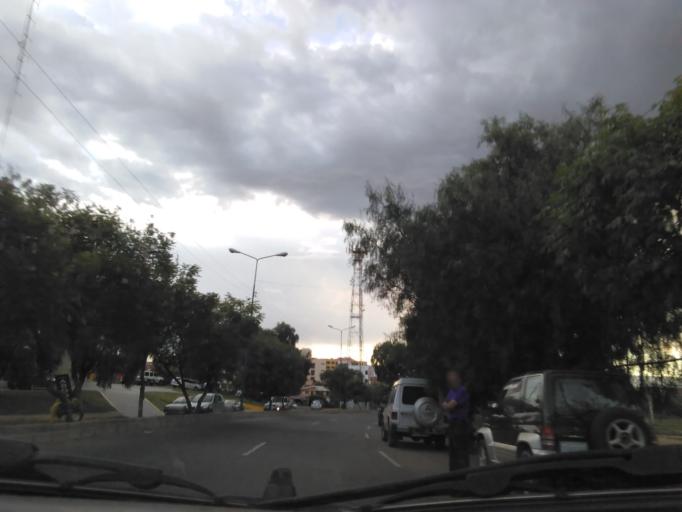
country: BO
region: Cochabamba
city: Cochabamba
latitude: -17.3614
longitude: -66.1730
